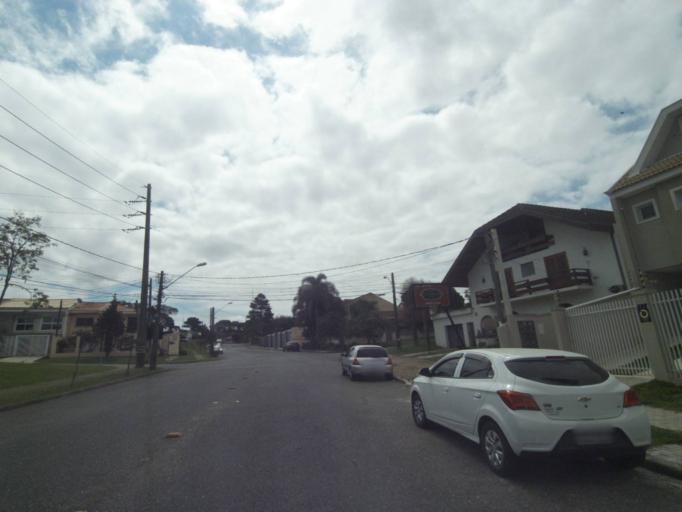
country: BR
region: Parana
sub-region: Curitiba
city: Curitiba
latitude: -25.4016
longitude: -49.2822
